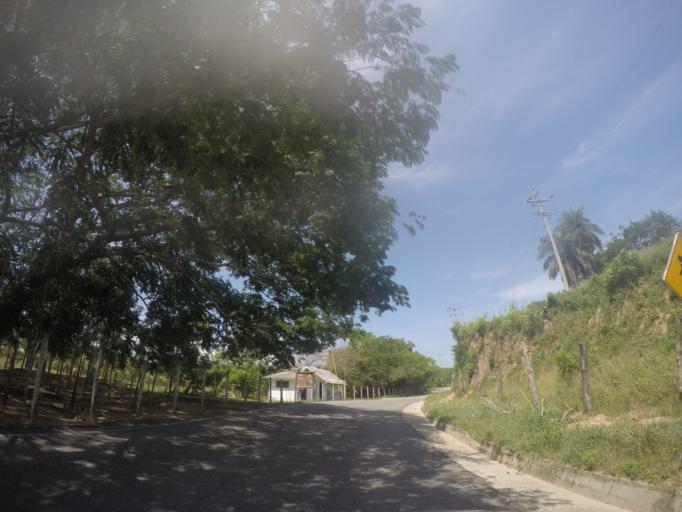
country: MX
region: Oaxaca
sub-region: Villa de Tututepec de Melchor Ocampo
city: Santa Rosa de Lima
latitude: 15.9904
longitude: -97.5417
